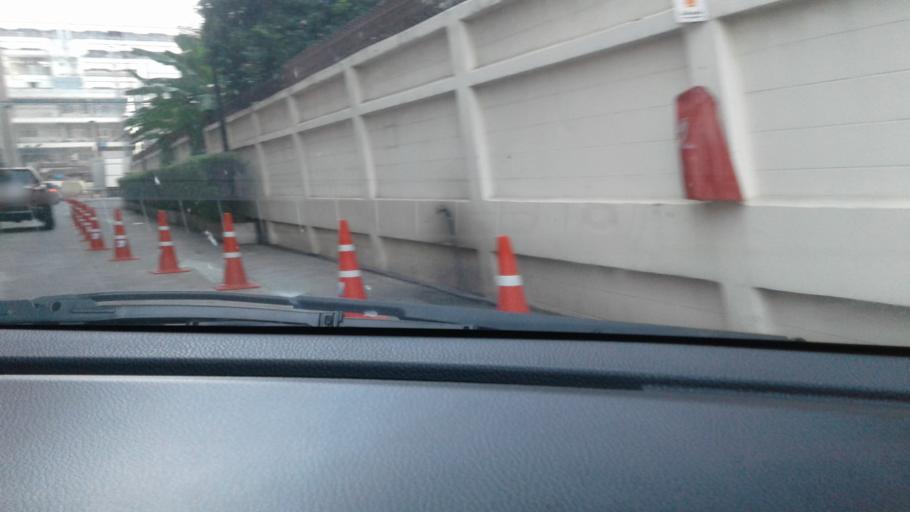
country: TH
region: Bangkok
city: Dusit
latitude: 13.7694
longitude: 100.5279
